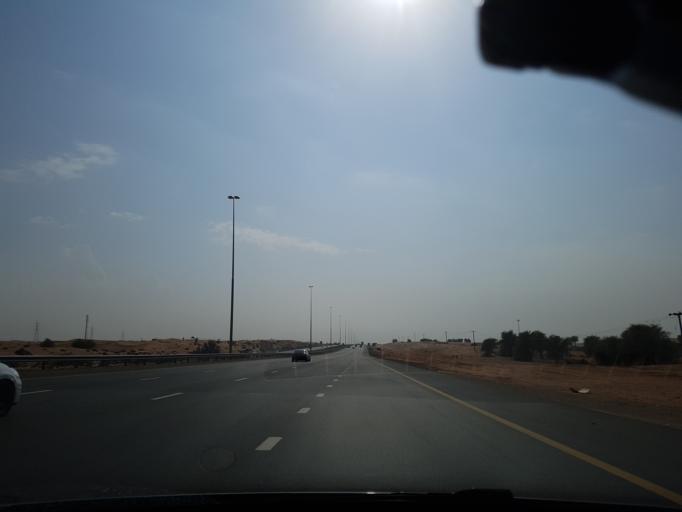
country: AE
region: Umm al Qaywayn
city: Umm al Qaywayn
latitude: 25.5247
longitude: 55.7195
